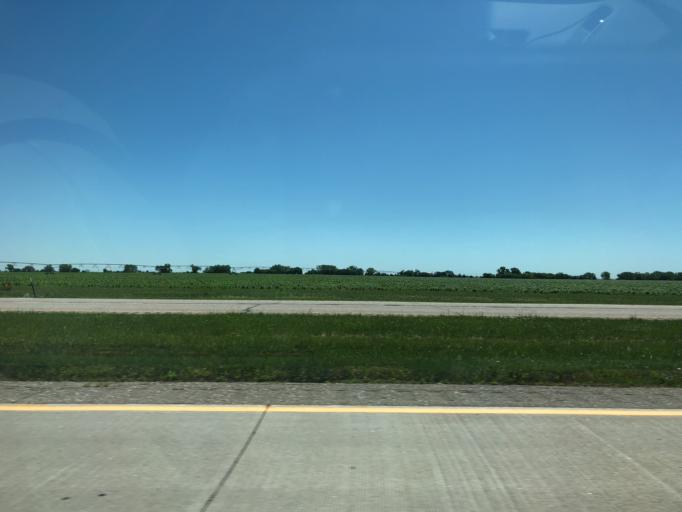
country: US
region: Nebraska
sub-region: York County
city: York
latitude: 40.7972
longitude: -97.5977
